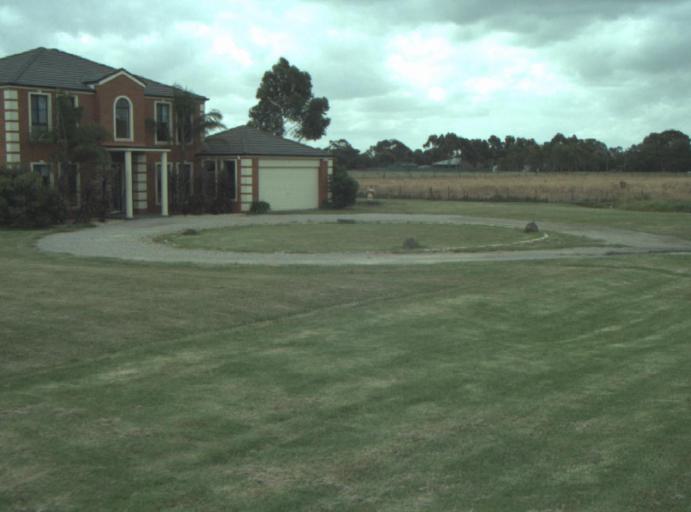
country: AU
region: Victoria
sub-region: Greater Geelong
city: East Geelong
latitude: -38.1753
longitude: 144.4138
